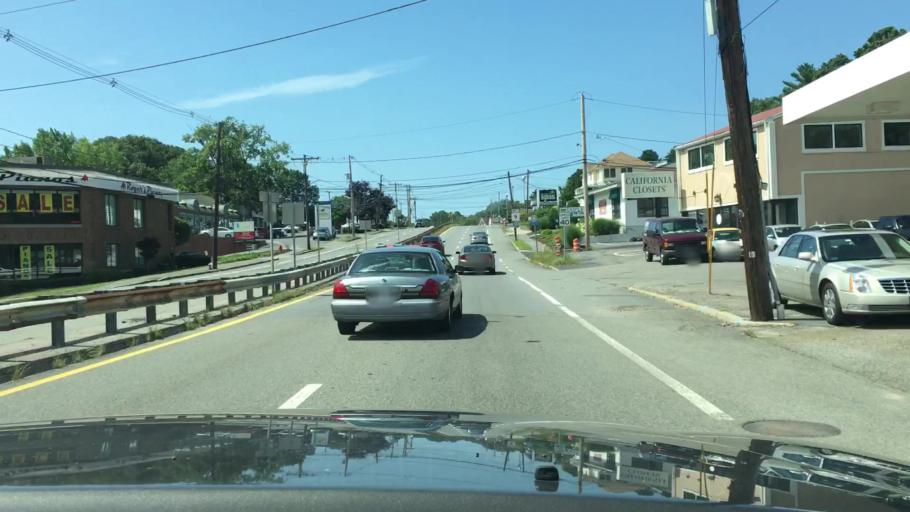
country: US
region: Massachusetts
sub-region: Middlesex County
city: Natick
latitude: 42.3045
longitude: -71.3262
